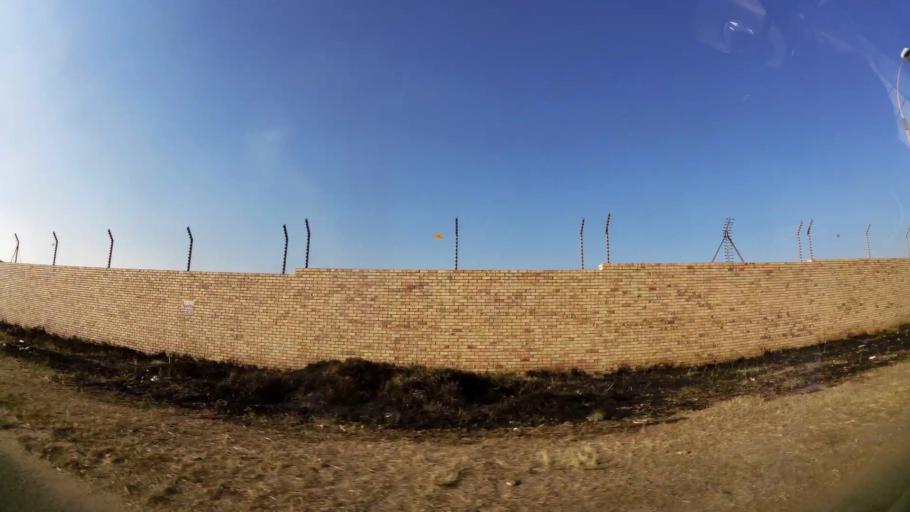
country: ZA
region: Gauteng
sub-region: West Rand District Municipality
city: Randfontein
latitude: -26.2010
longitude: 27.6955
